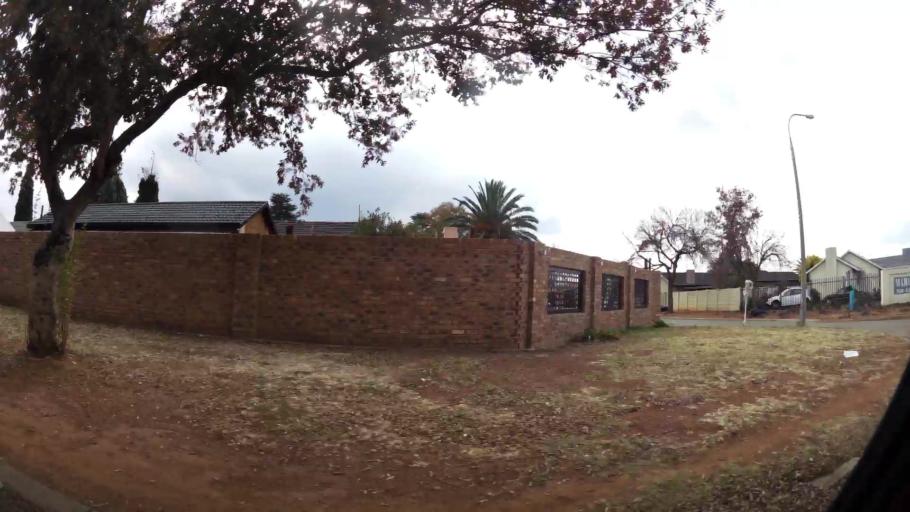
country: ZA
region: Gauteng
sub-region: Sedibeng District Municipality
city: Vanderbijlpark
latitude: -26.7247
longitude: 27.8518
